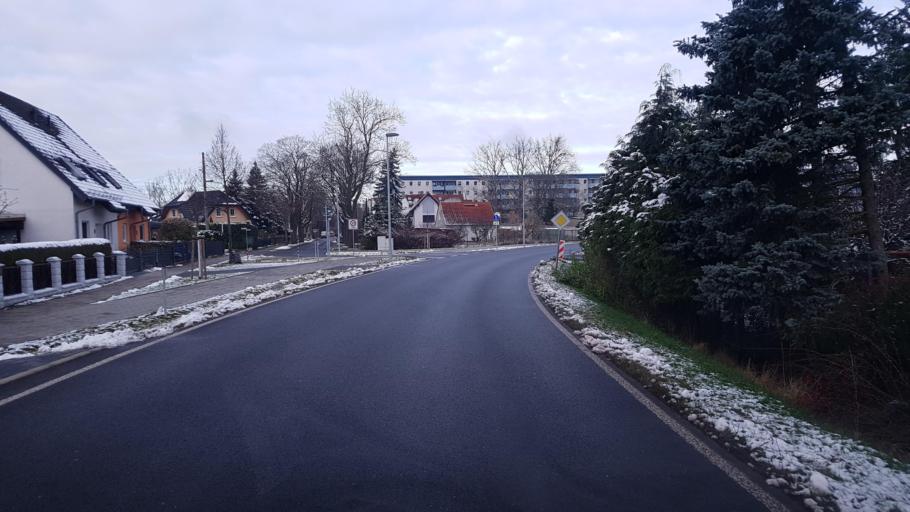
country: DE
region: Brandenburg
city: Strausberg
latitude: 52.5710
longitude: 13.8942
